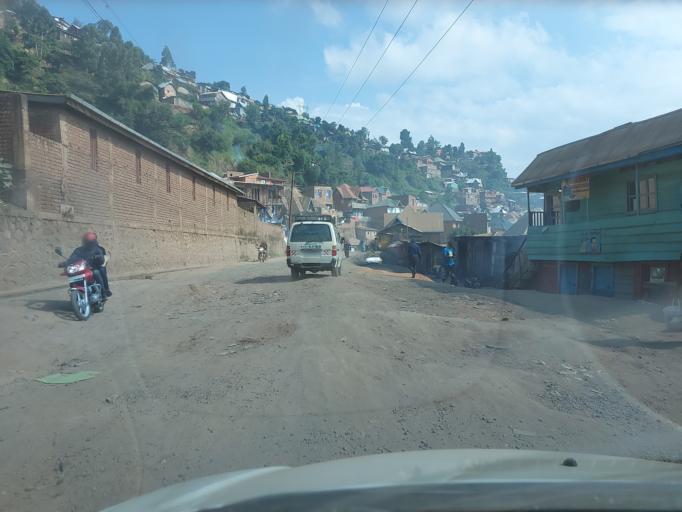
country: CD
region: South Kivu
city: Bukavu
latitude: -2.5112
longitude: 28.8483
